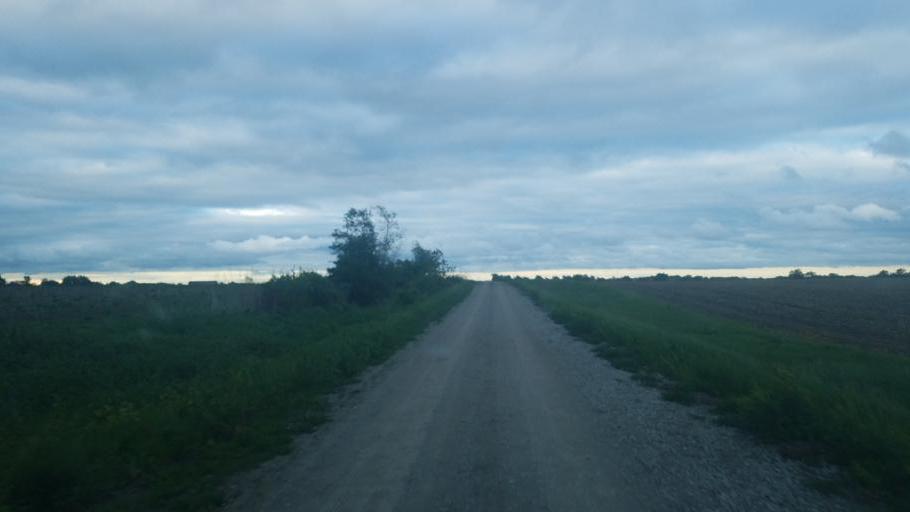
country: US
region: Iowa
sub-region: Decatur County
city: Lamoni
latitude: 40.5948
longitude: -93.9646
